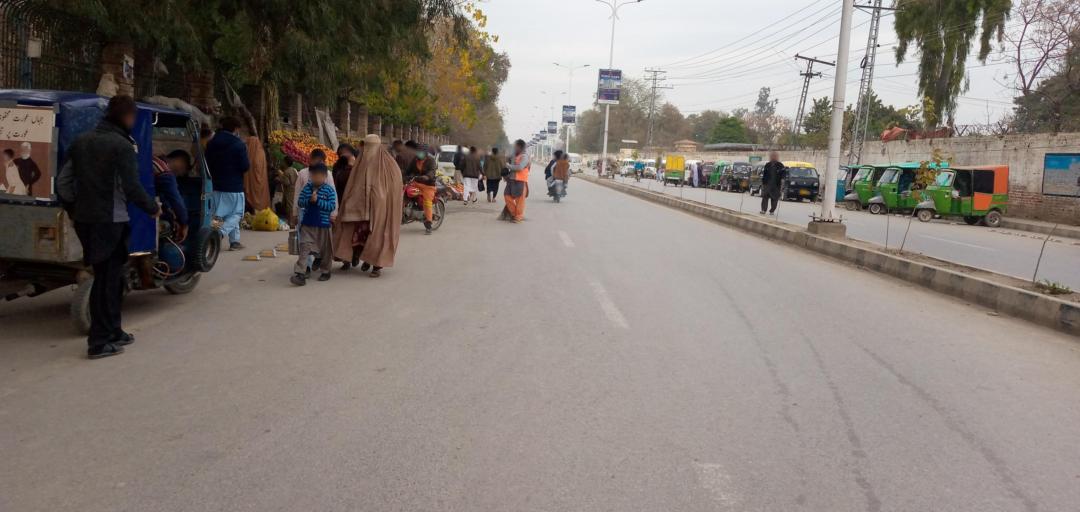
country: PK
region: Khyber Pakhtunkhwa
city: Peshawar
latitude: 33.9984
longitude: 71.4884
